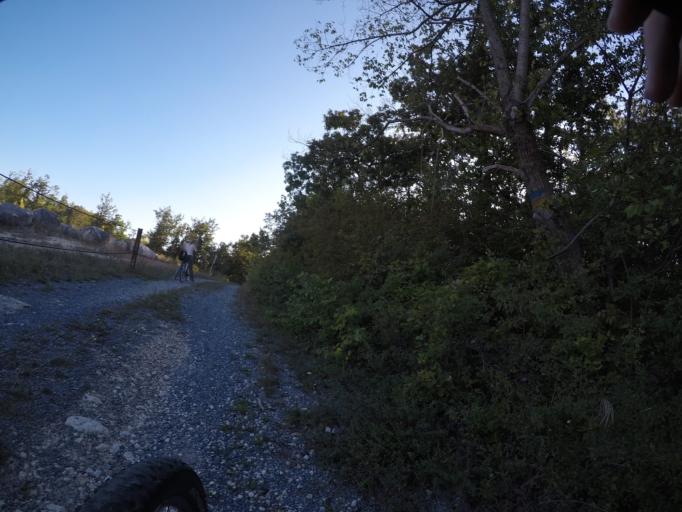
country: AT
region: Lower Austria
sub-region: Politischer Bezirk Bruck an der Leitha
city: Mannersdorf am Leithagebirge
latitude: 47.9617
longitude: 16.6012
